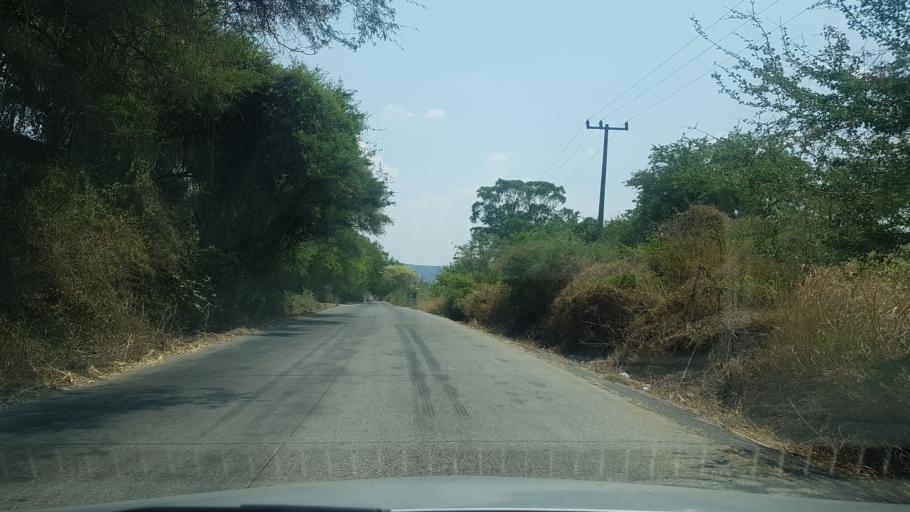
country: MX
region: Morelos
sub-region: Tlaltizapan de Zapata
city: Colonia Palo Prieto (Chipitongo)
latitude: 18.7530
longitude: -99.1132
